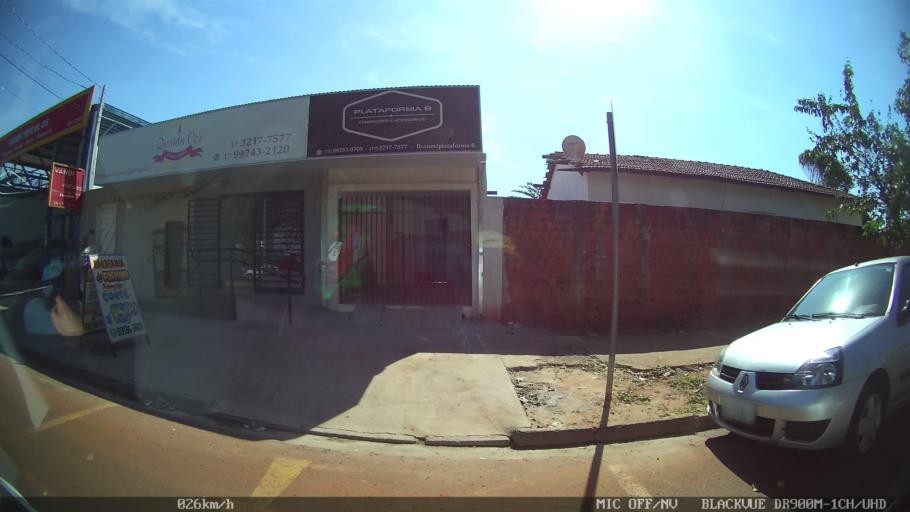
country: BR
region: Sao Paulo
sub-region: Sao Jose Do Rio Preto
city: Sao Jose do Rio Preto
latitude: -20.7847
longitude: -49.3971
